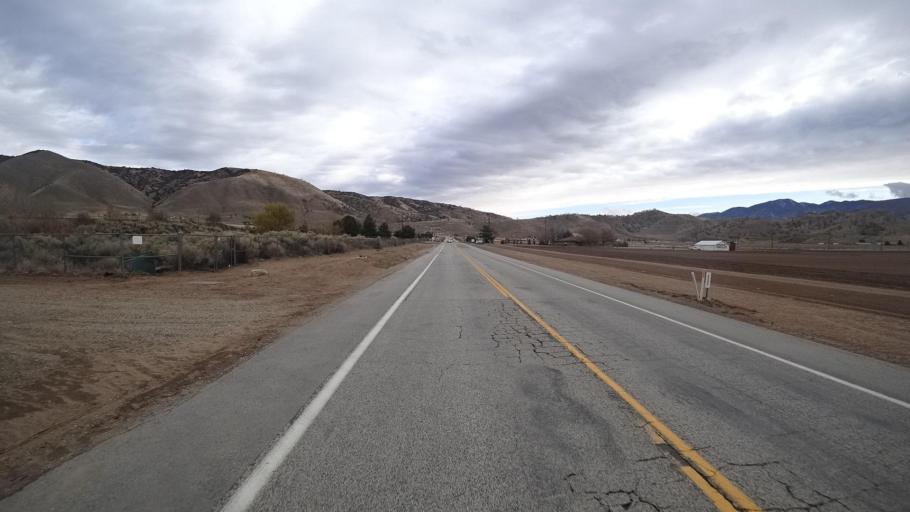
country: US
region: California
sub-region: Kern County
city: Bear Valley Springs
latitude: 35.1309
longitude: -118.5768
